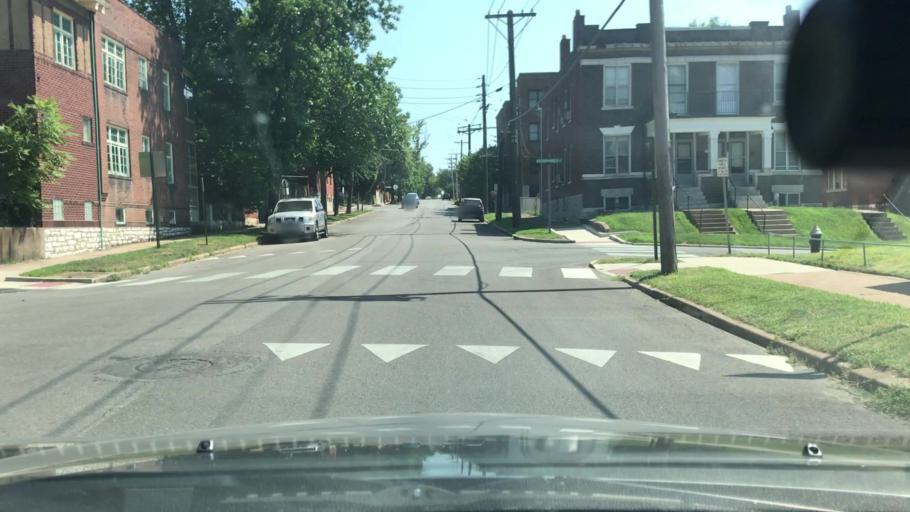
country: US
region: Missouri
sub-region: City of Saint Louis
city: St. Louis
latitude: 38.5990
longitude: -90.2503
